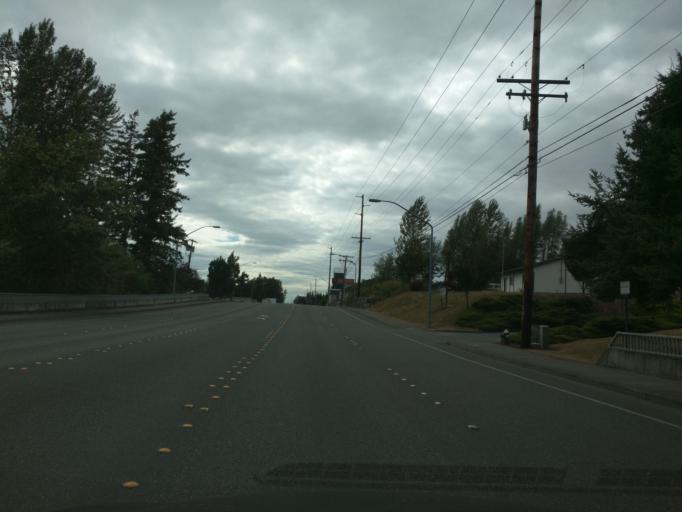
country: US
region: Washington
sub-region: Whatcom County
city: Bellingham
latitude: 48.7897
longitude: -122.4822
